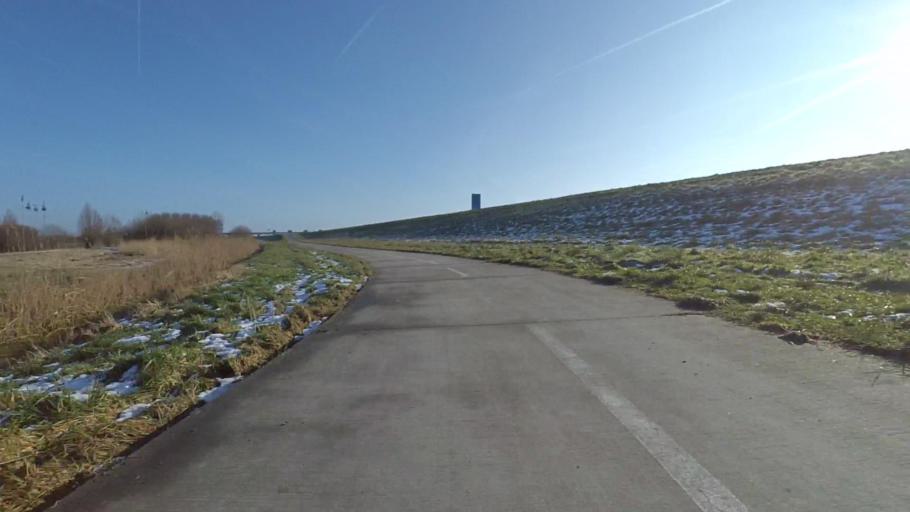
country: NL
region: Gelderland
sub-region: Gemeente Nijkerk
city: Nijkerk
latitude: 52.2631
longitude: 5.4632
